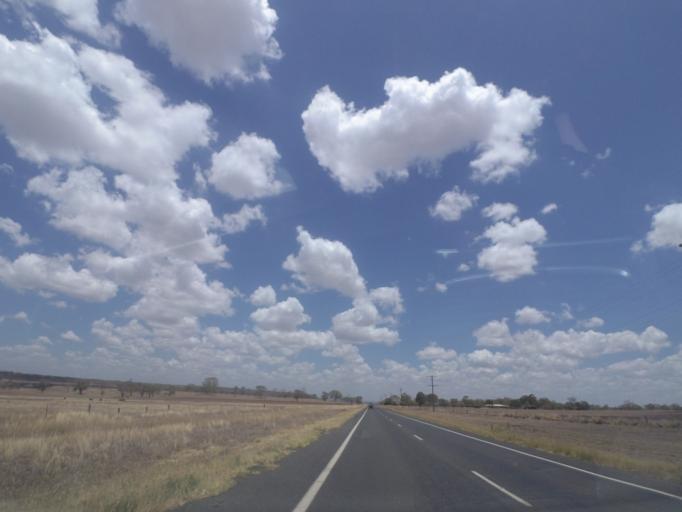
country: AU
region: Queensland
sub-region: Southern Downs
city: Warwick
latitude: -27.9885
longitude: 151.9993
